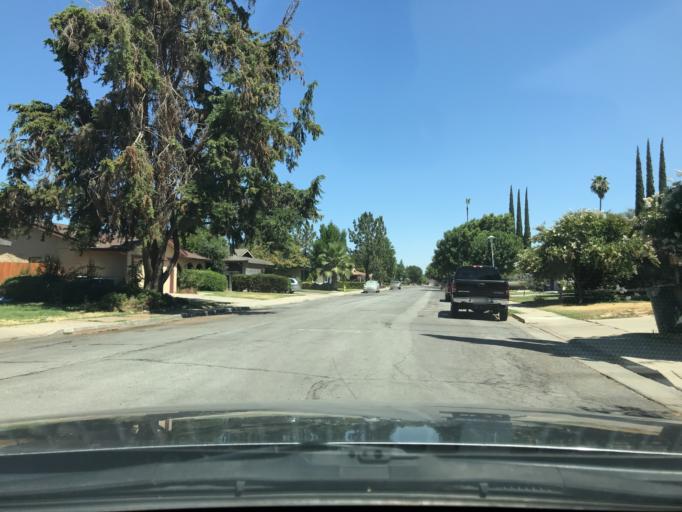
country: US
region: California
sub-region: Merced County
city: Merced
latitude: 37.3254
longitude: -120.4794
